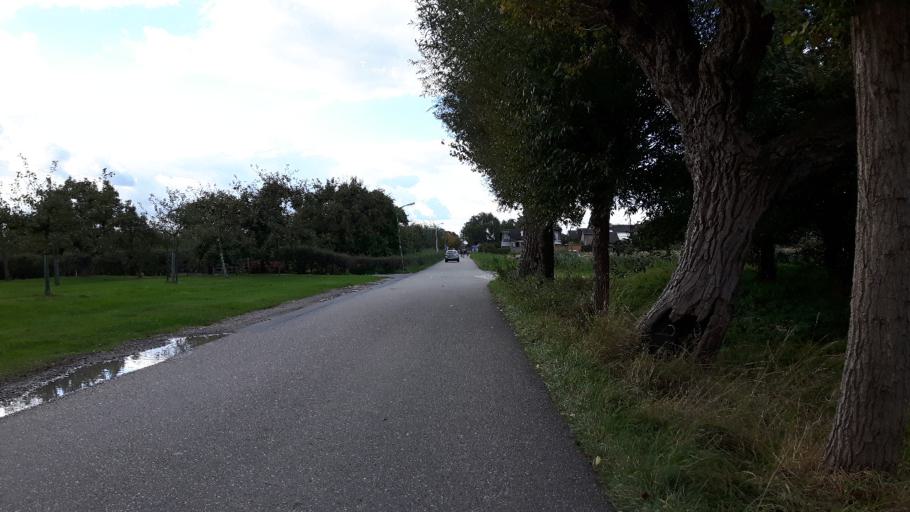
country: NL
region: South Holland
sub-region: Gemeente Leerdam
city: Leerdam
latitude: 51.9179
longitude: 5.1229
